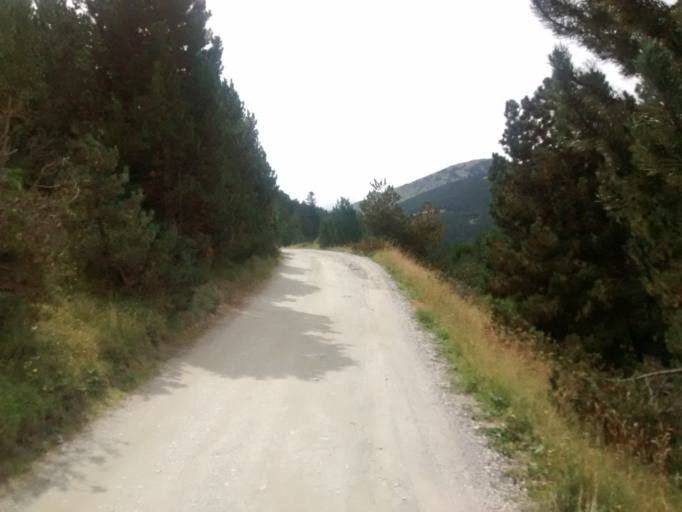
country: ES
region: Catalonia
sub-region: Provincia de Lleida
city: Vielha
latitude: 42.7511
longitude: 0.9876
